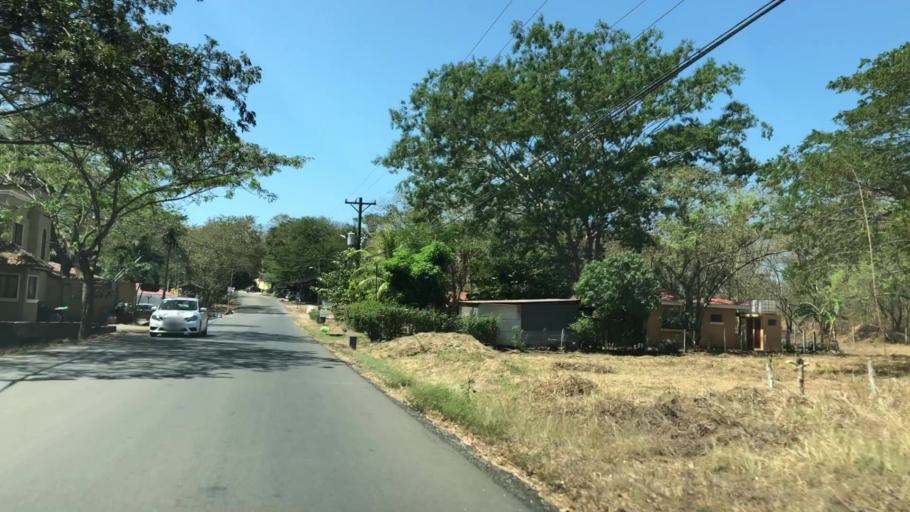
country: CR
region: Guanacaste
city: Sardinal
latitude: 10.3427
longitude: -85.8445
